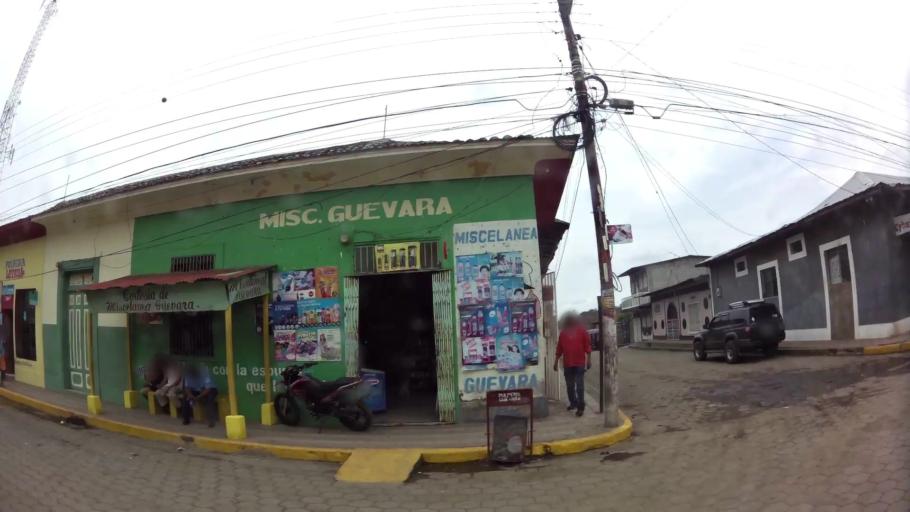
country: NI
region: Granada
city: Nandaime
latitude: 11.7560
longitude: -86.0529
